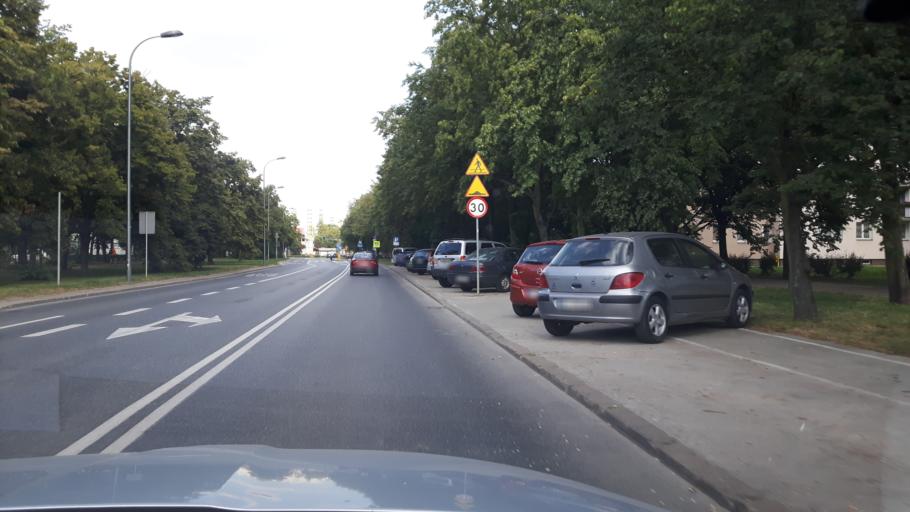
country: PL
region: Masovian Voivodeship
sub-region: Warszawa
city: Targowek
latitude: 52.2962
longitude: 21.0383
